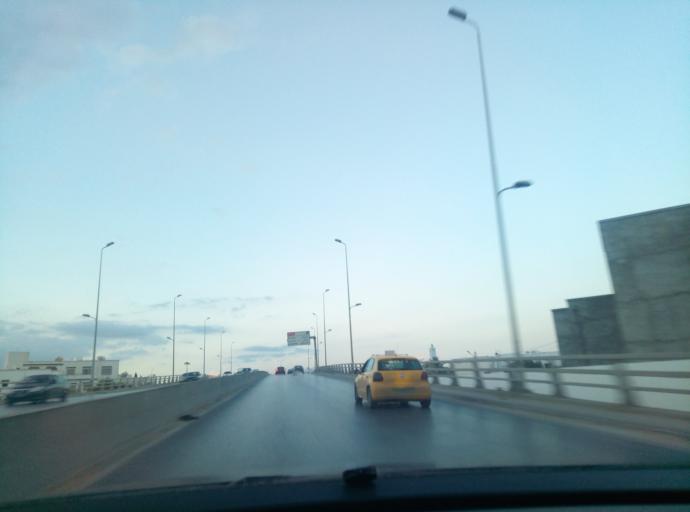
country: TN
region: Manouba
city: Manouba
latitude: 36.8090
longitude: 10.1190
